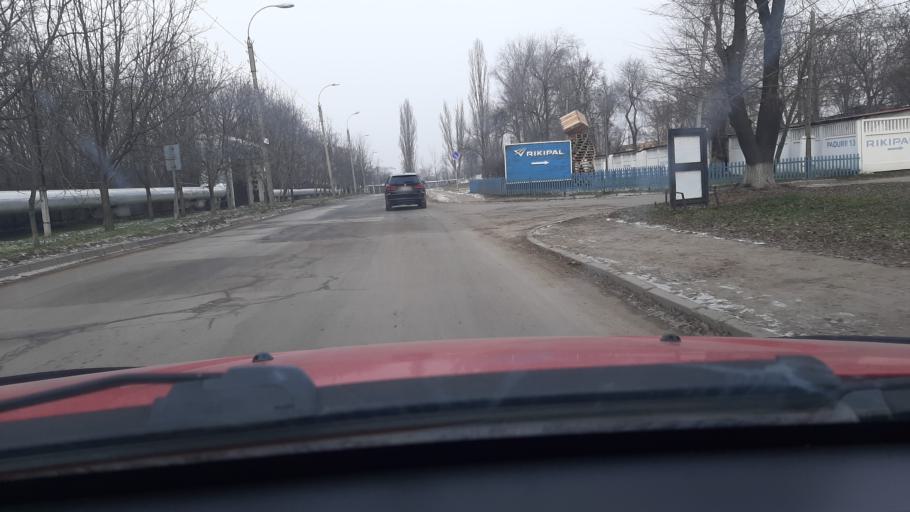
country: MD
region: Chisinau
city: Chisinau
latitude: 46.9759
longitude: 28.8937
